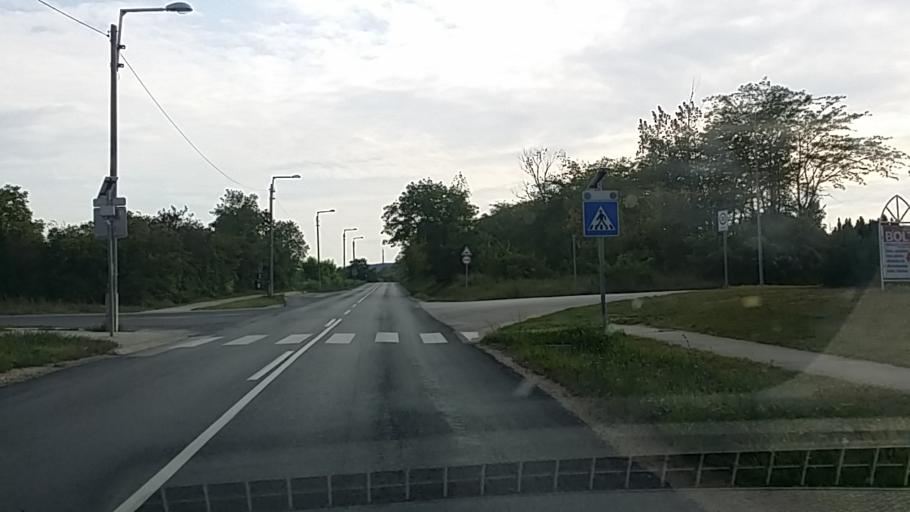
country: HU
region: Gyor-Moson-Sopron
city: Fertorakos
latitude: 47.7152
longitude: 16.6140
